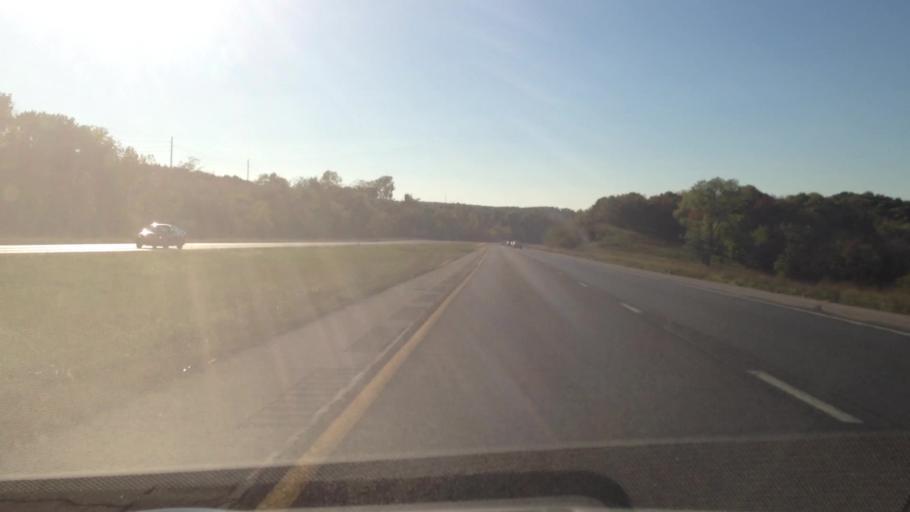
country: US
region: Kansas
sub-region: Johnson County
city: De Soto
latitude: 38.9475
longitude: -94.8912
